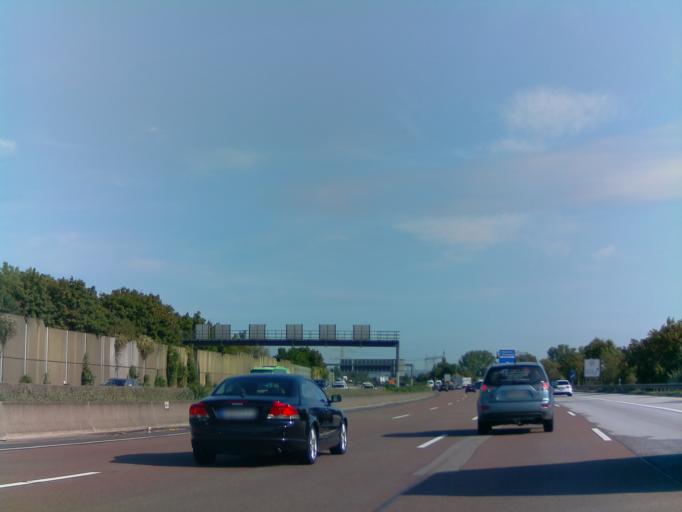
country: DE
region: Hesse
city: Niederrad
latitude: 50.0814
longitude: 8.6181
